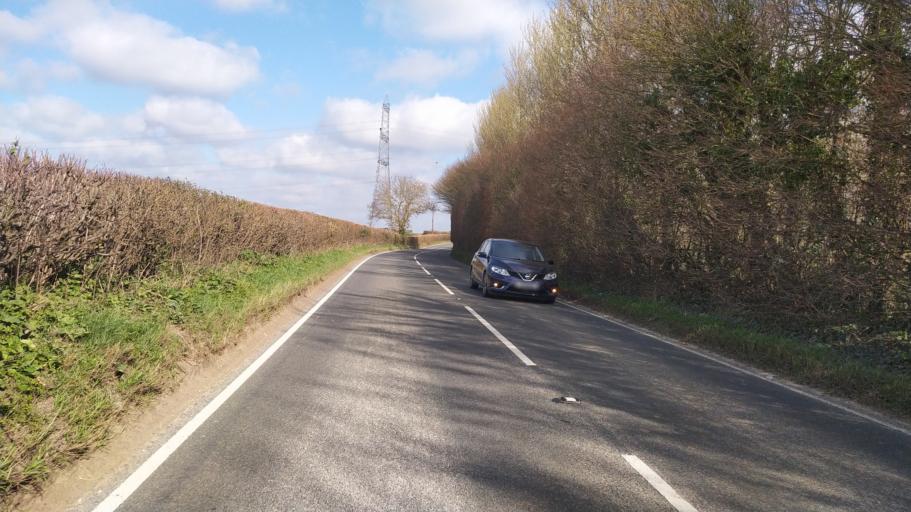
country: GB
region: England
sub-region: Dorset
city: Bridport
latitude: 50.7544
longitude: -2.7387
